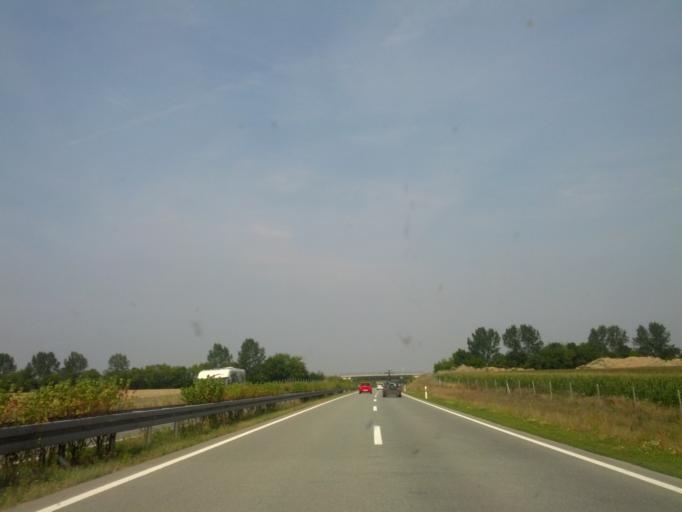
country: DE
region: Mecklenburg-Vorpommern
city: Wittenhagen
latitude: 54.1330
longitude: 13.1594
